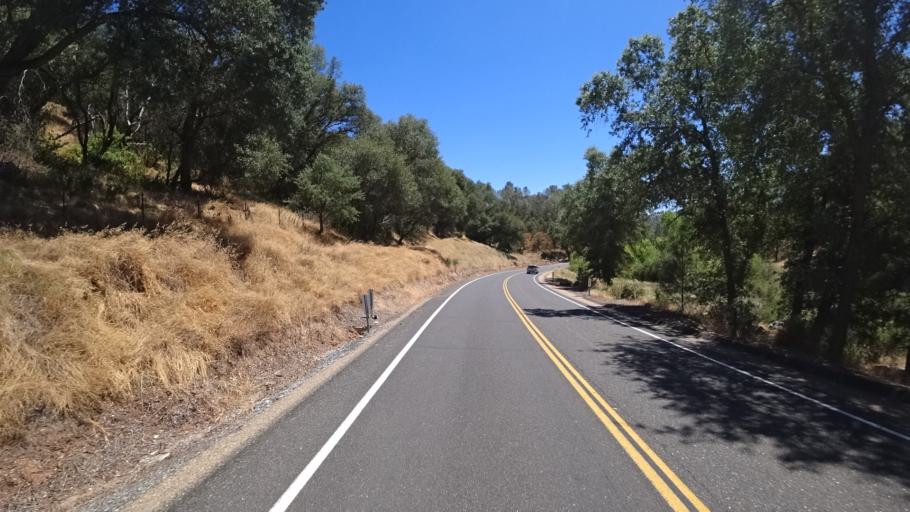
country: US
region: California
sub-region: Calaveras County
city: San Andreas
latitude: 38.1687
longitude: -120.6719
